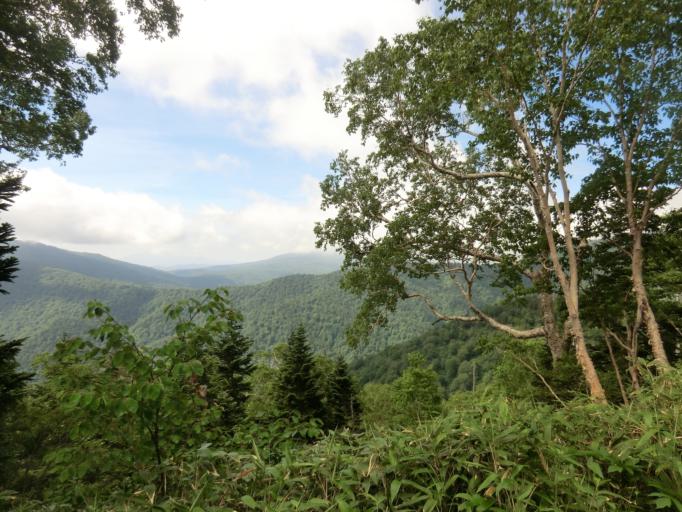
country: JP
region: Gunma
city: Numata
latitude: 36.8834
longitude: 139.1854
